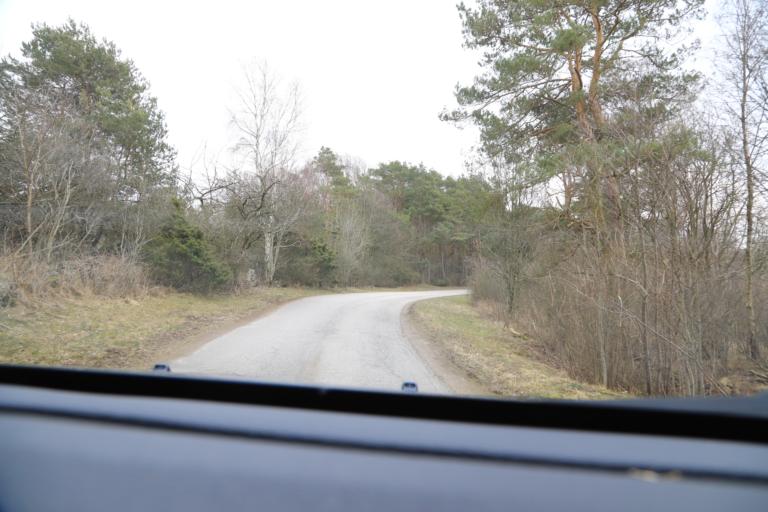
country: SE
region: Halland
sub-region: Kungsbacka Kommun
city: Frillesas
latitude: 57.2608
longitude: 12.1232
